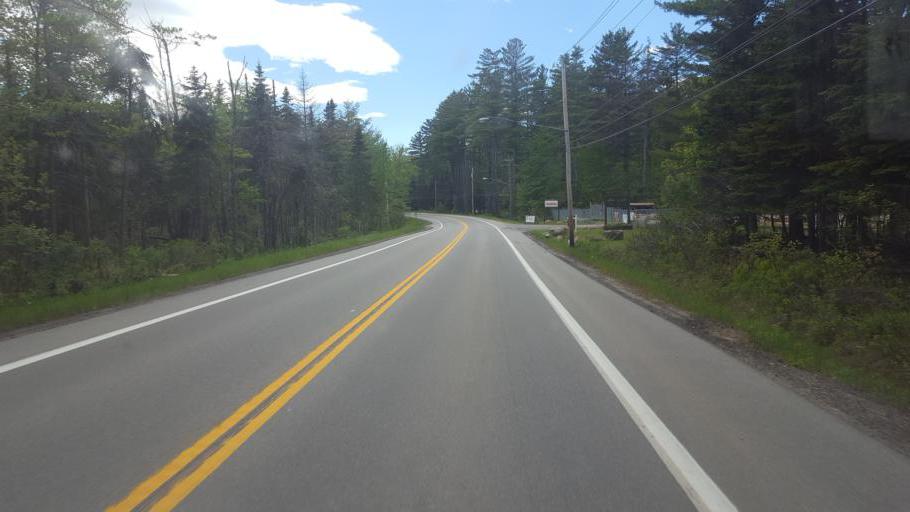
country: US
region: New York
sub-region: Hamilton County
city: Lake Pleasant
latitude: 43.4831
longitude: -74.3862
